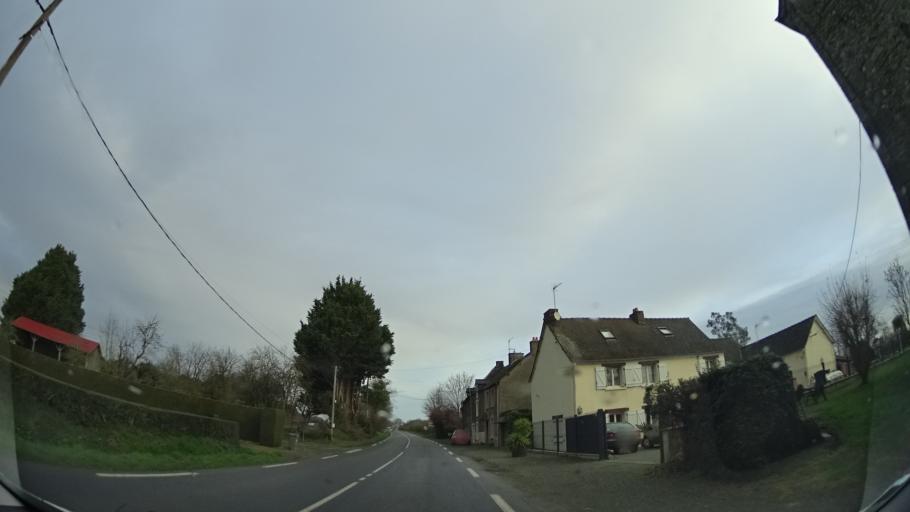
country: FR
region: Brittany
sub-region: Departement des Cotes-d'Armor
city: Evran
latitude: 48.3959
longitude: -1.9798
